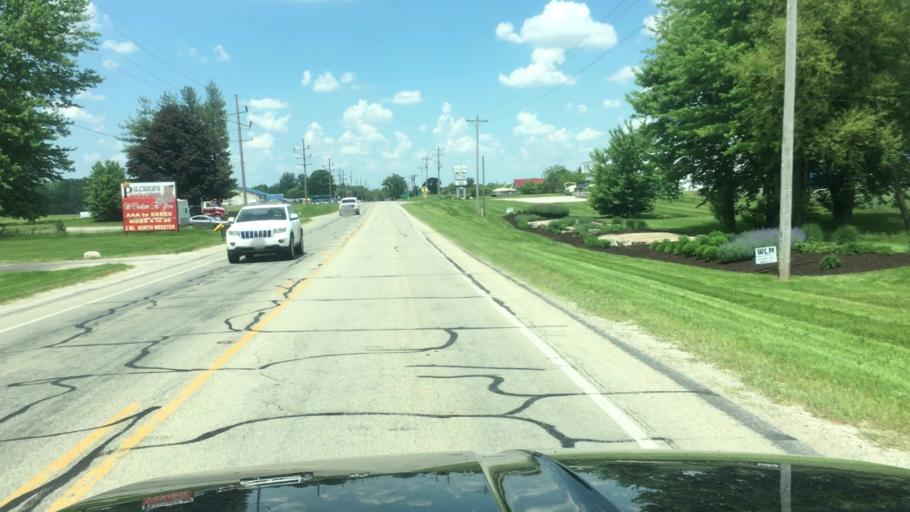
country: US
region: Indiana
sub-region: Kosciusko County
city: North Webster
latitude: 41.3042
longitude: -85.6908
